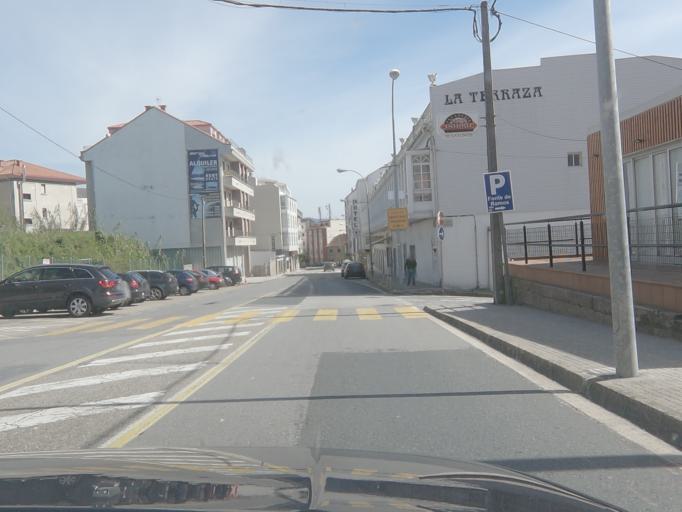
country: ES
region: Galicia
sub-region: Provincia de Pontevedra
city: Sanxenxo
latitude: 42.4032
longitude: -8.8091
